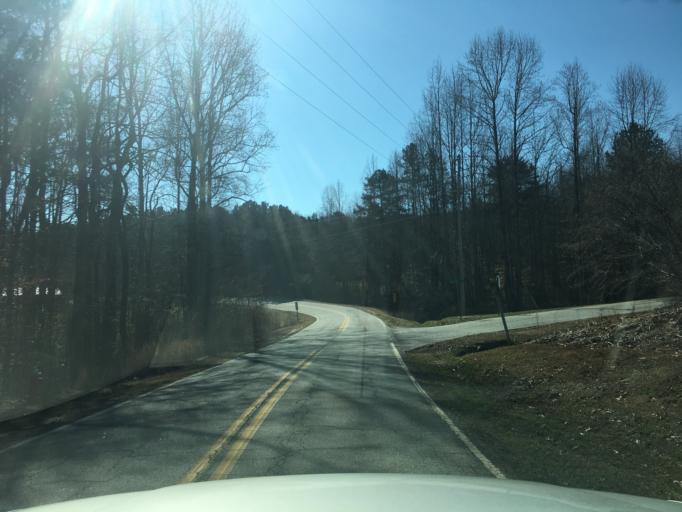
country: US
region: South Carolina
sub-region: Pickens County
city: Pickens
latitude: 34.8357
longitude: -82.7896
